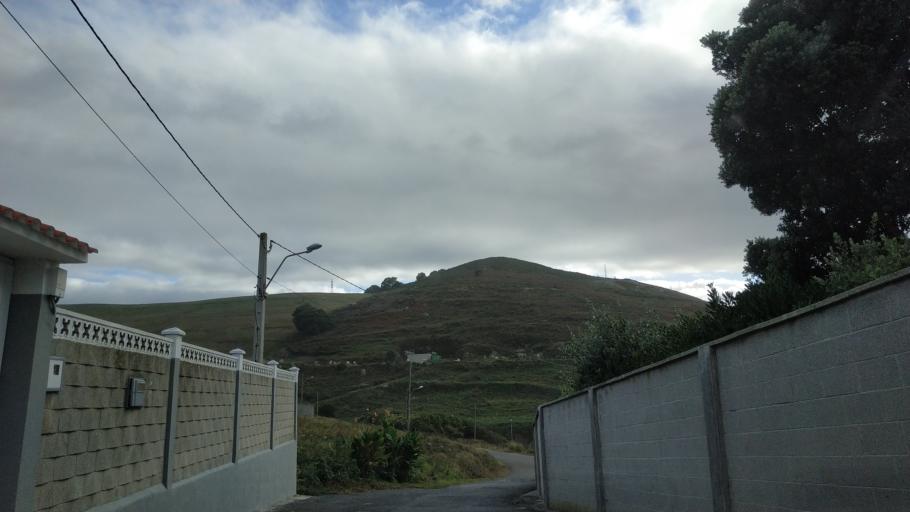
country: ES
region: Galicia
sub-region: Provincia da Coruna
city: A Coruna
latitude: 43.3741
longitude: -8.4456
